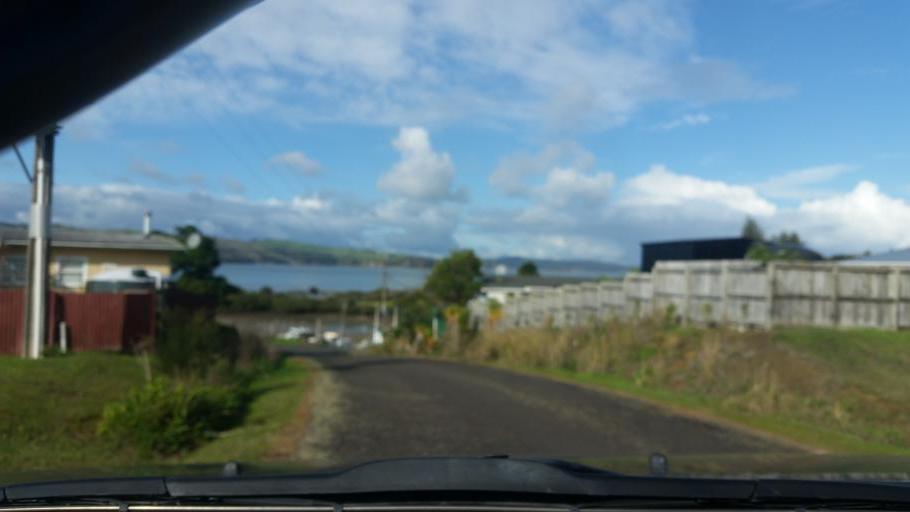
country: NZ
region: Auckland
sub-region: Auckland
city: Wellsford
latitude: -36.2472
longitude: 174.2467
